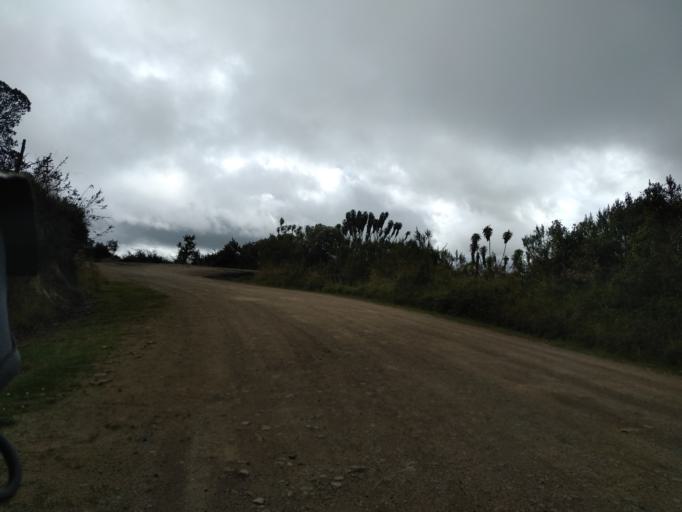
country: EC
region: Carchi
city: Tulcan
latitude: 0.7409
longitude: -77.7865
